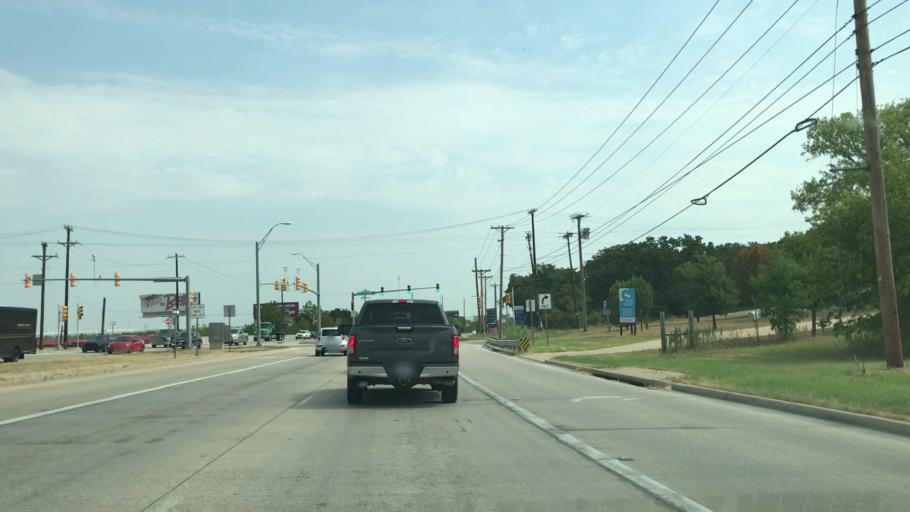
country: US
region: Texas
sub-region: Tarrant County
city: Keller
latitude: 32.9557
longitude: -97.2542
